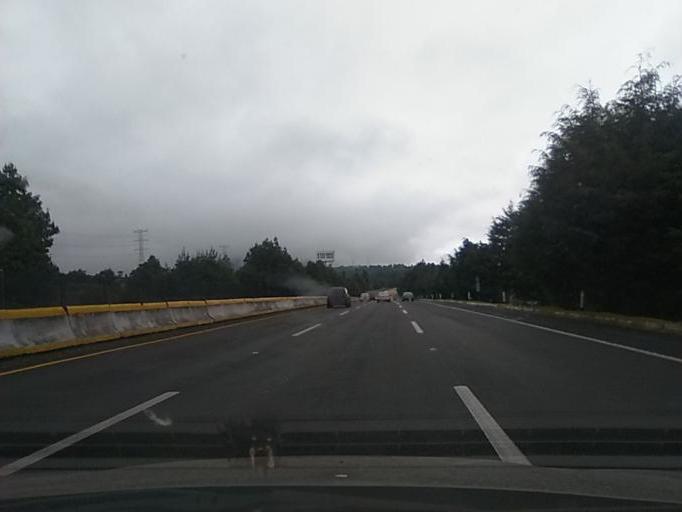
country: MX
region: Morelos
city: Tres Marias
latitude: 19.1186
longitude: -99.1815
